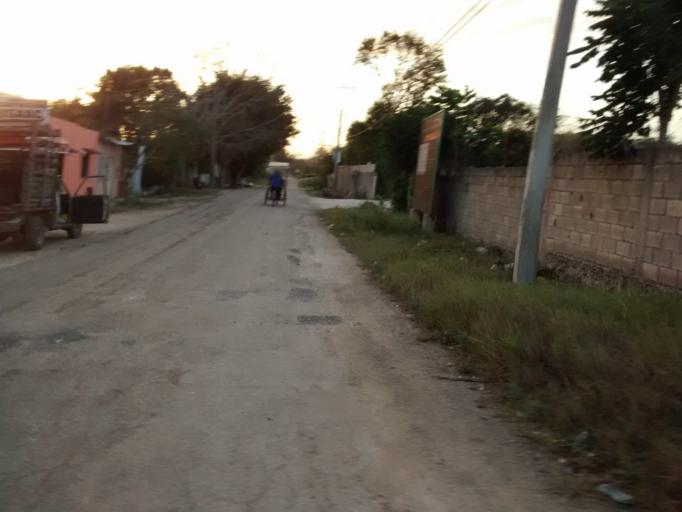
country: MX
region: Yucatan
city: Valladolid
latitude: 20.6848
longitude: -88.1805
